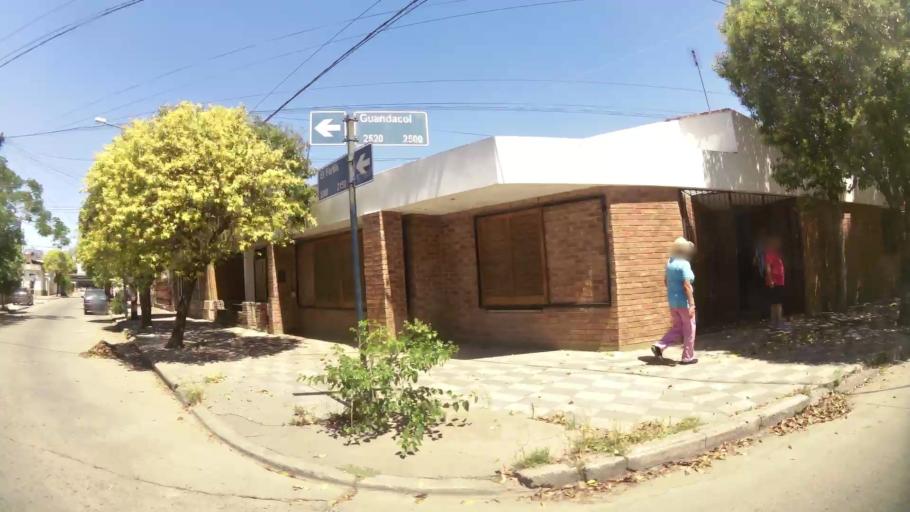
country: AR
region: Cordoba
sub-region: Departamento de Capital
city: Cordoba
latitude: -31.4381
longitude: -64.1270
